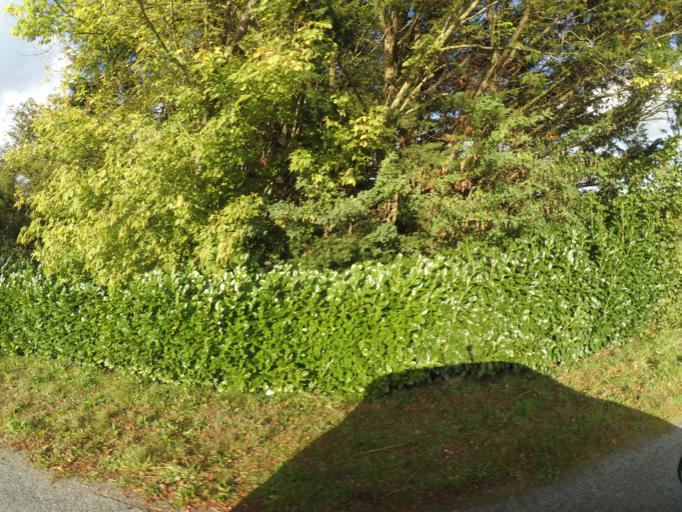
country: FR
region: Brittany
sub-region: Departement du Morbihan
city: Peillac
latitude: 47.7257
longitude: -2.2381
